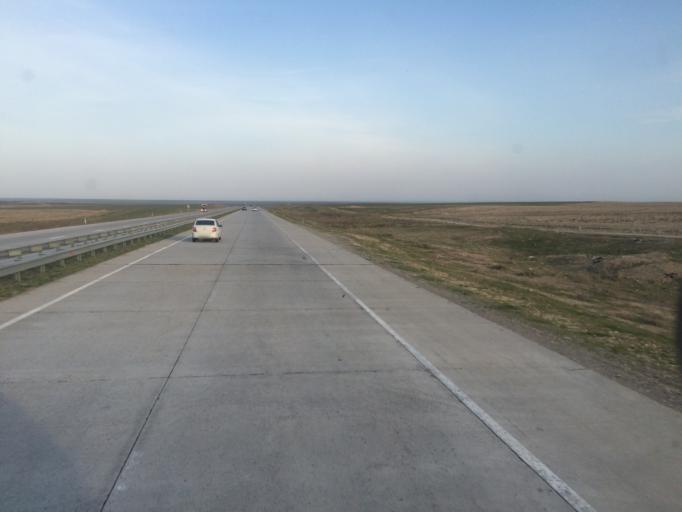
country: KZ
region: Ongtustik Qazaqstan
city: Temirlanovka
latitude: 42.6467
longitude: 69.2456
